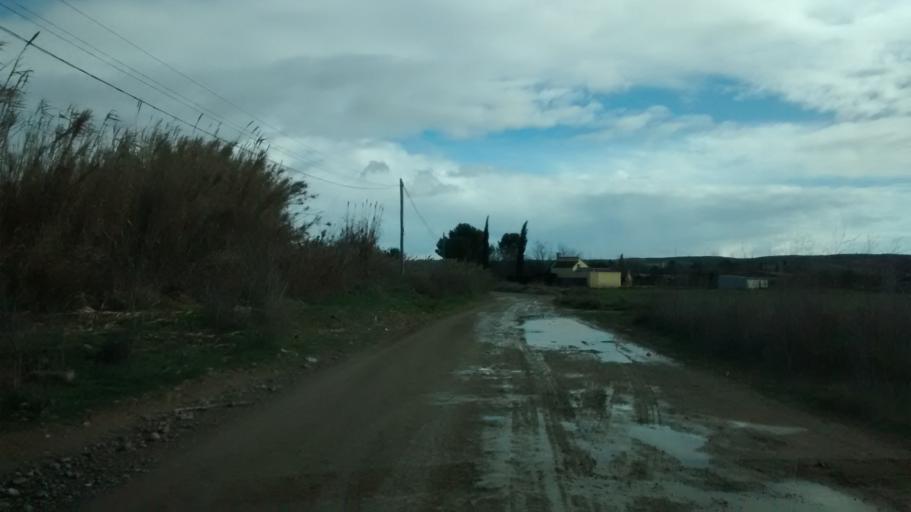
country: ES
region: Aragon
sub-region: Provincia de Zaragoza
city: Villanueva de Gallego
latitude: 41.7423
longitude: -0.7925
